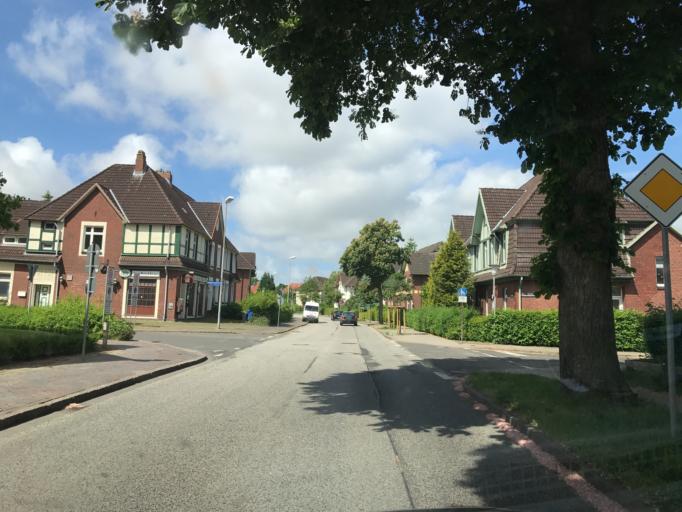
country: DE
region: Schleswig-Holstein
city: Brunsbuttel
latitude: 53.8977
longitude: 9.1411
